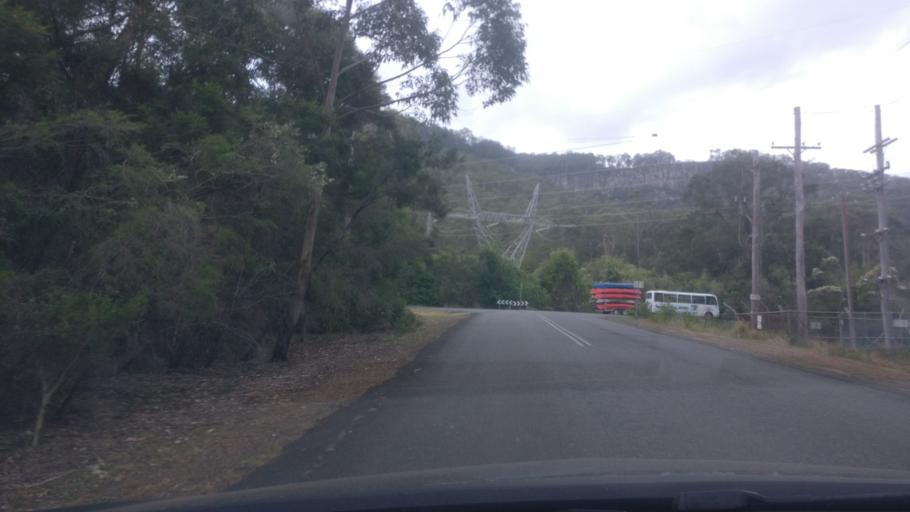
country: AU
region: New South Wales
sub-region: Shoalhaven Shire
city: Kangaroo Valley
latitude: -34.7259
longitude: 150.4822
